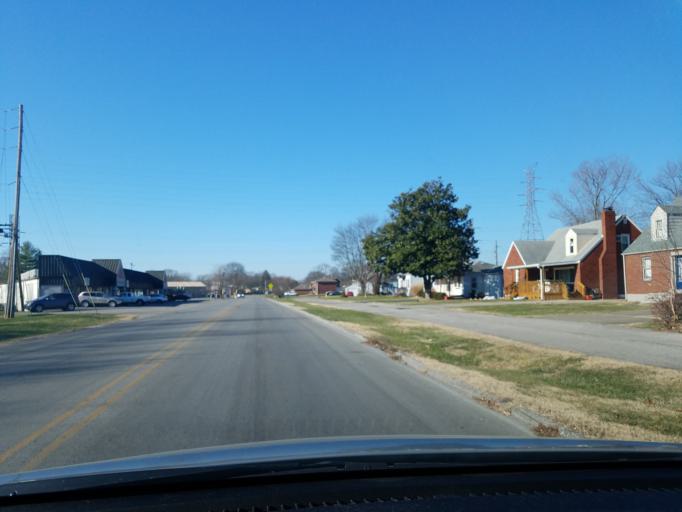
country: US
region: Indiana
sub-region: Clark County
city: Clarksville
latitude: 38.3051
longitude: -85.7800
